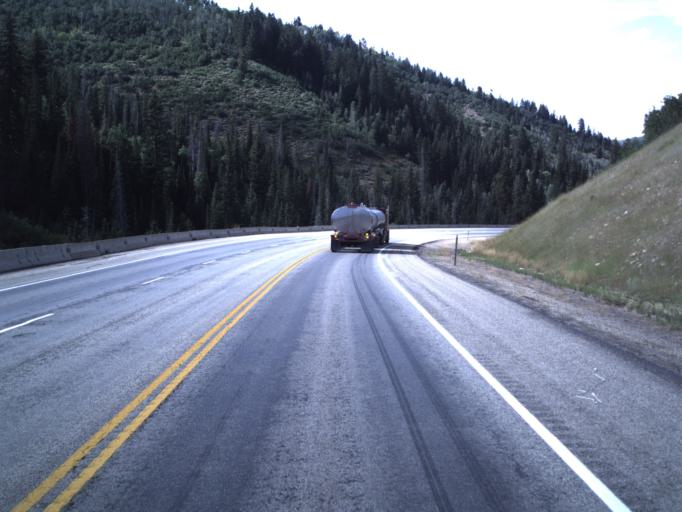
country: US
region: Utah
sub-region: Wasatch County
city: Heber
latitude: 40.3235
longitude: -111.2610
